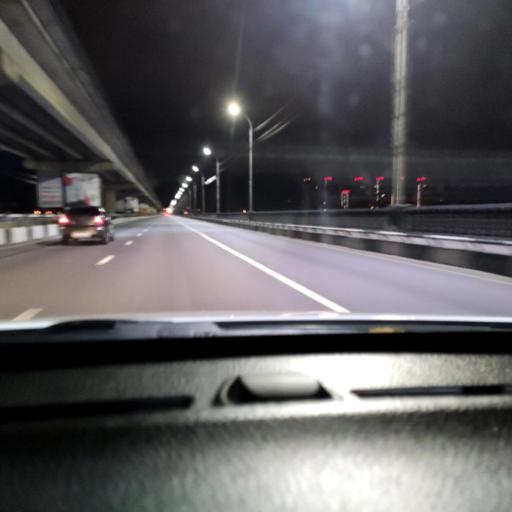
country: RU
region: Voronezj
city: Voronezh
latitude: 51.6924
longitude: 39.2394
